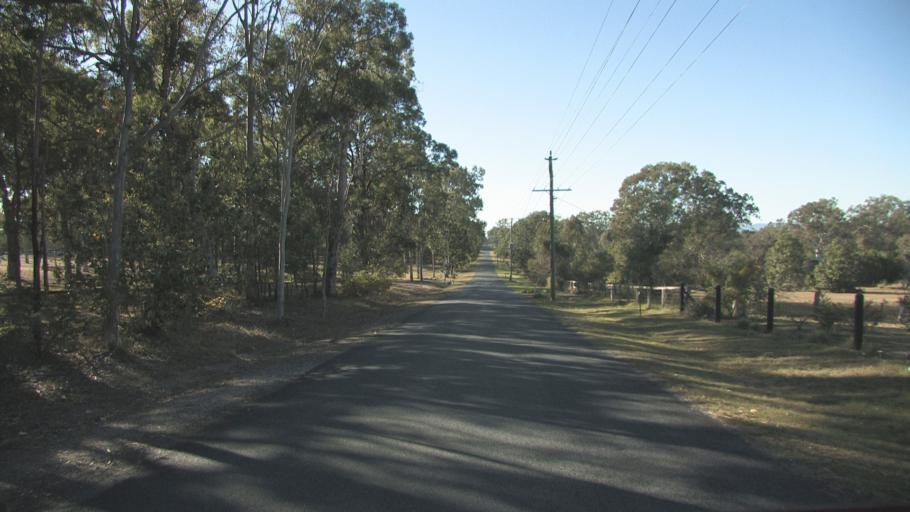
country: AU
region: Queensland
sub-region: Logan
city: North Maclean
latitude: -27.7872
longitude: 152.9635
